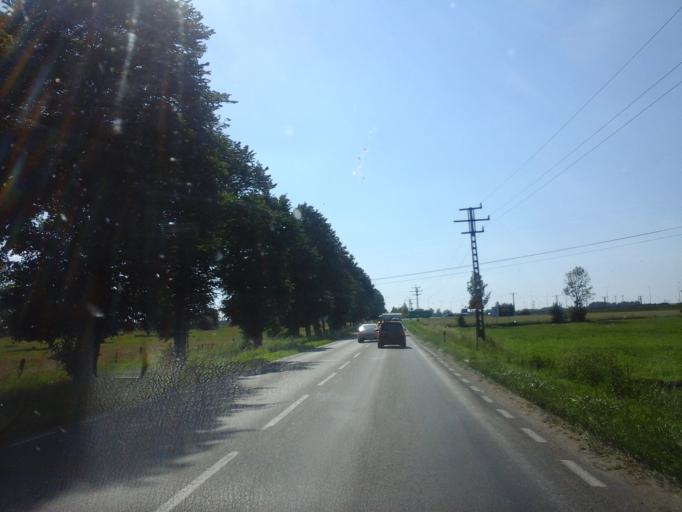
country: PL
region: West Pomeranian Voivodeship
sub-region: Powiat bialogardzki
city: Karlino
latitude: 54.0302
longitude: 15.8974
